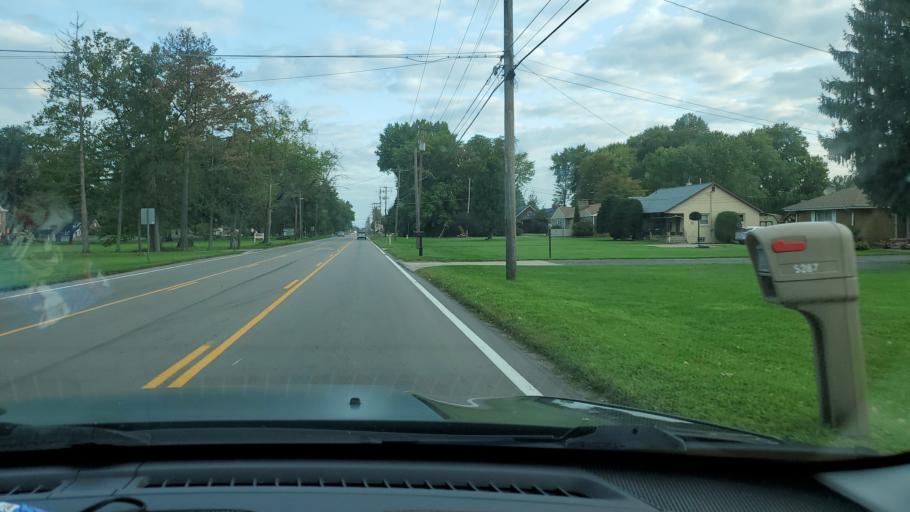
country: US
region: Ohio
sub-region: Mahoning County
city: Struthers
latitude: 41.0405
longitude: -80.6156
